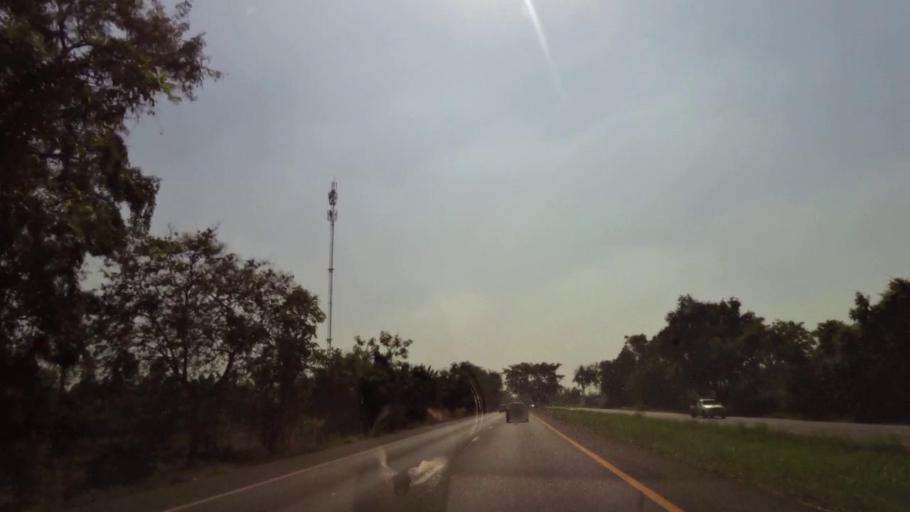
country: TH
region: Phichit
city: Bueng Na Rang
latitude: 16.0404
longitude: 100.1179
